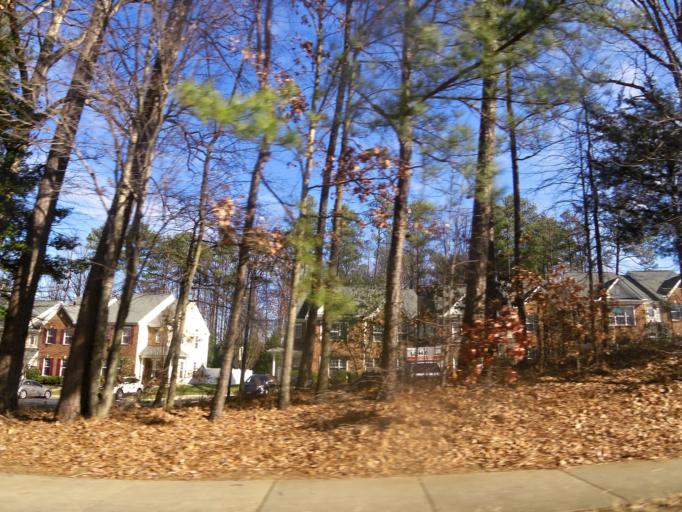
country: US
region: Virginia
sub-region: Henrico County
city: Tuckahoe
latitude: 37.6284
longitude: -77.5531
